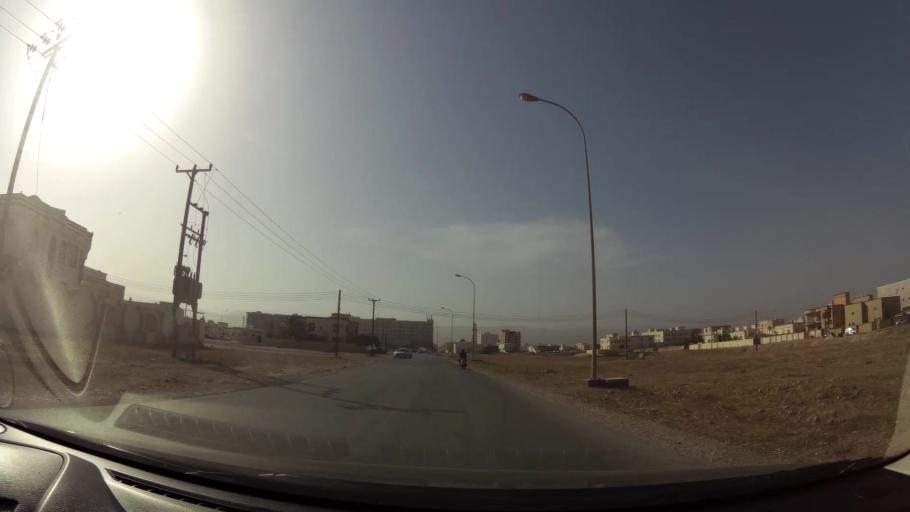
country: OM
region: Zufar
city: Salalah
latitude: 17.0056
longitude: 54.0235
